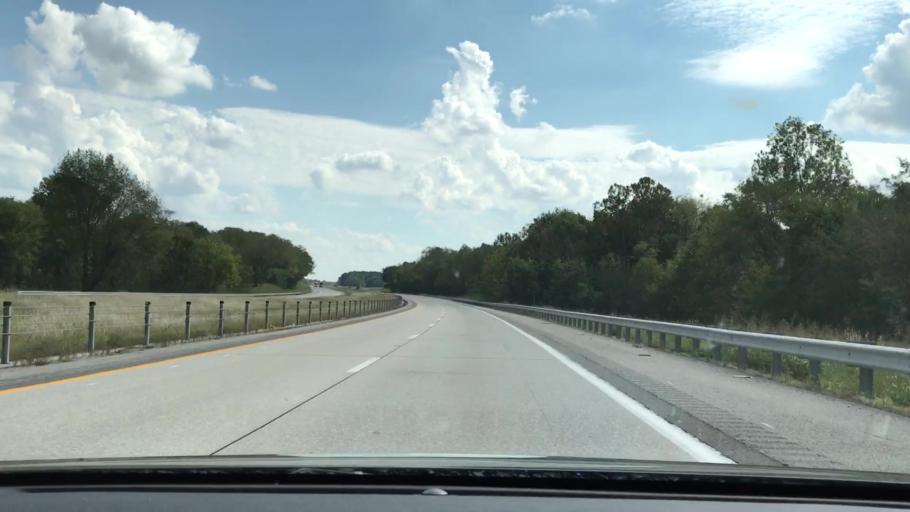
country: US
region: Kentucky
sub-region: Trigg County
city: Cadiz
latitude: 36.8532
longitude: -87.6994
